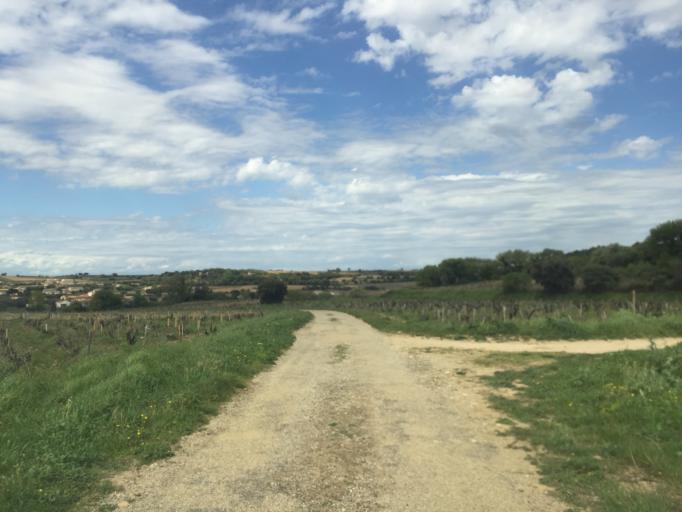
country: FR
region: Provence-Alpes-Cote d'Azur
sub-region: Departement du Vaucluse
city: Chateauneuf-du-Pape
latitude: 44.0576
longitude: 4.8501
